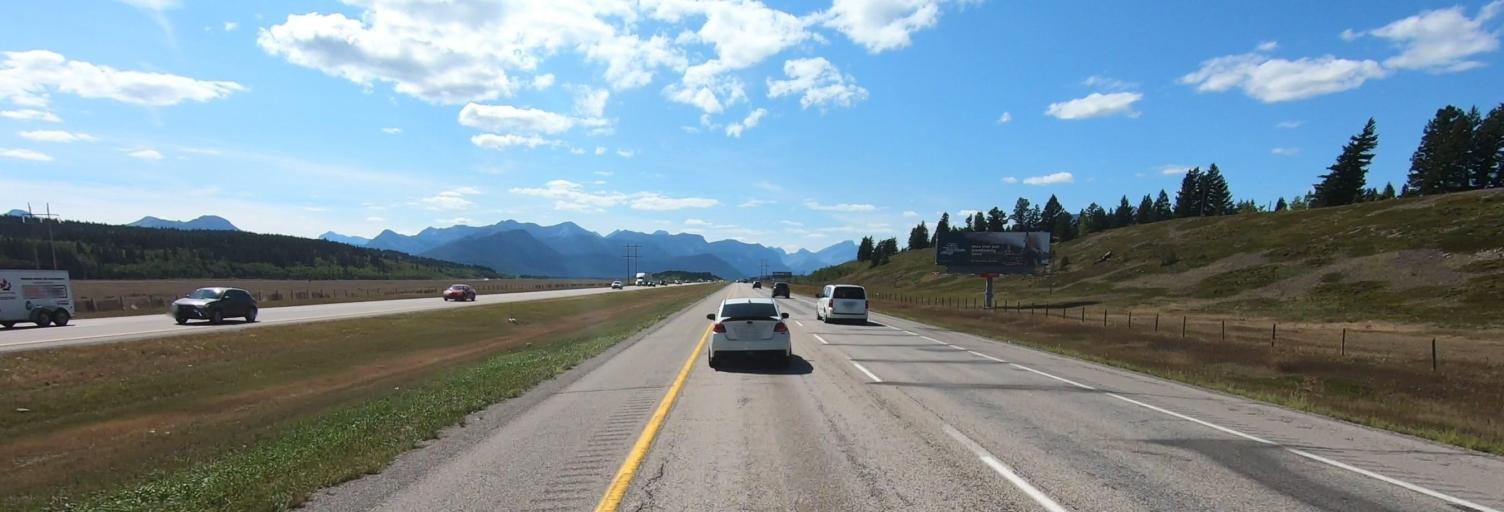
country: CA
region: Alberta
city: Canmore
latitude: 51.1255
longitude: -114.9631
